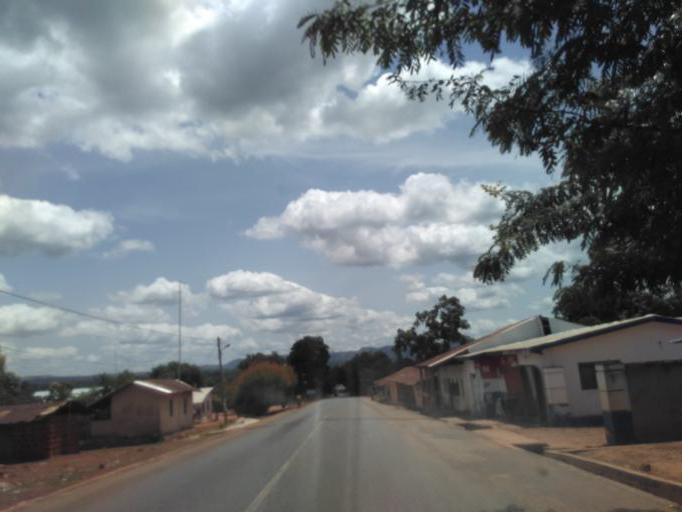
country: GH
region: Eastern
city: Koforidua
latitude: 6.1129
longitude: -0.1256
